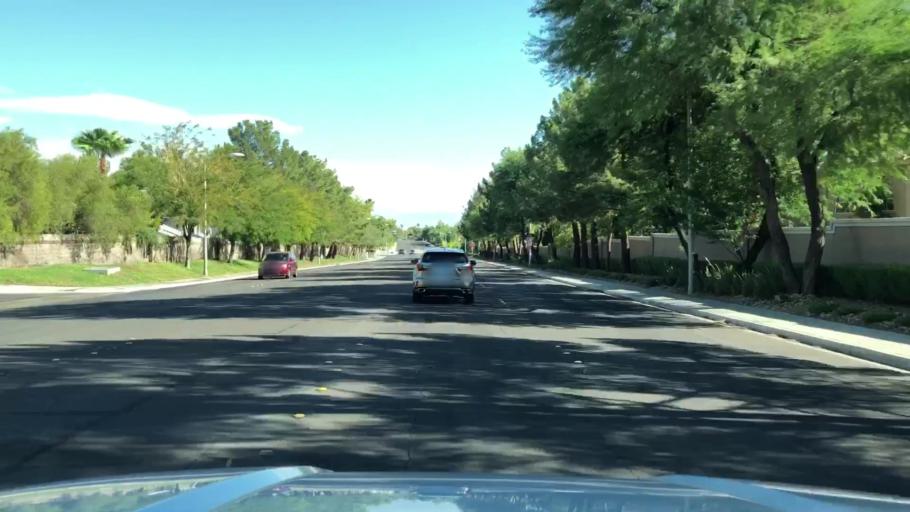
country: US
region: Nevada
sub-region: Clark County
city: Whitney
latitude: 36.0395
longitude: -115.0687
